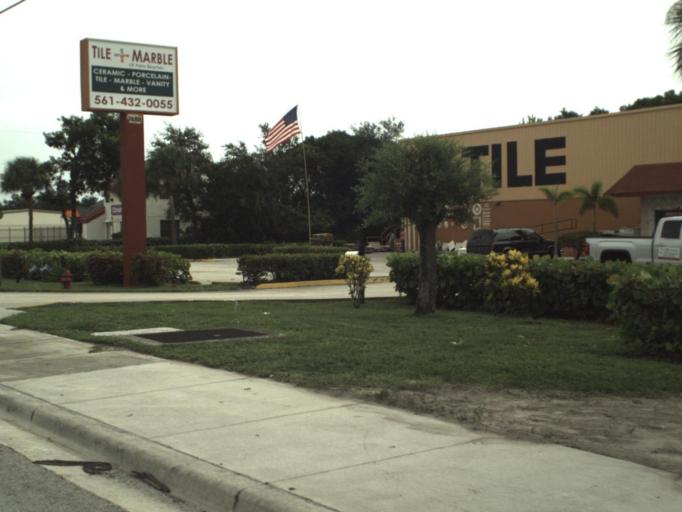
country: US
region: Florida
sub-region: Palm Beach County
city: Seminole Manor
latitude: 26.5645
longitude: -80.1139
